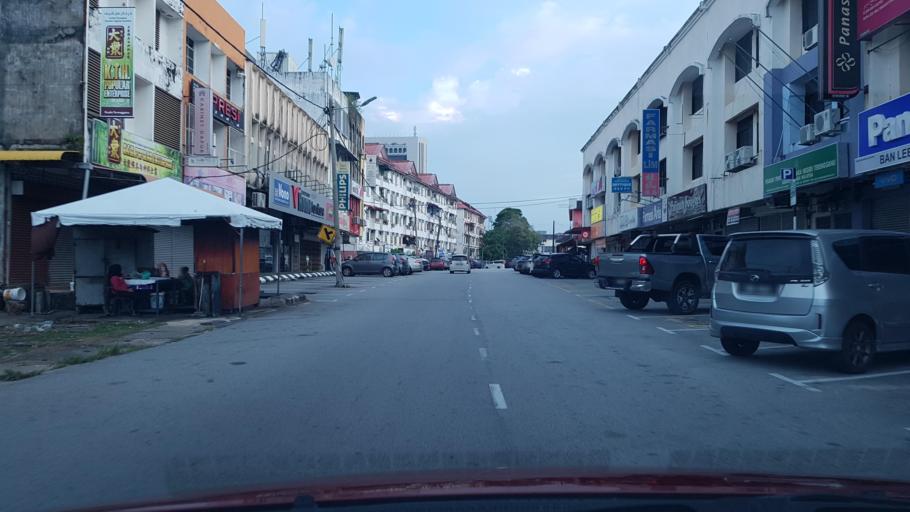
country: MY
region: Terengganu
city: Kuala Terengganu
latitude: 5.3358
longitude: 103.1410
